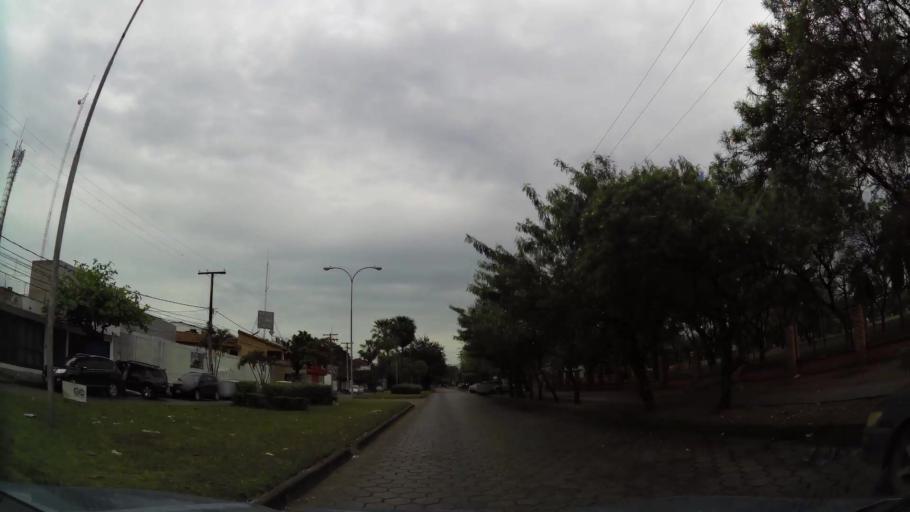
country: BO
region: Santa Cruz
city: Santa Cruz de la Sierra
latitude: -17.7925
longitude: -63.1730
